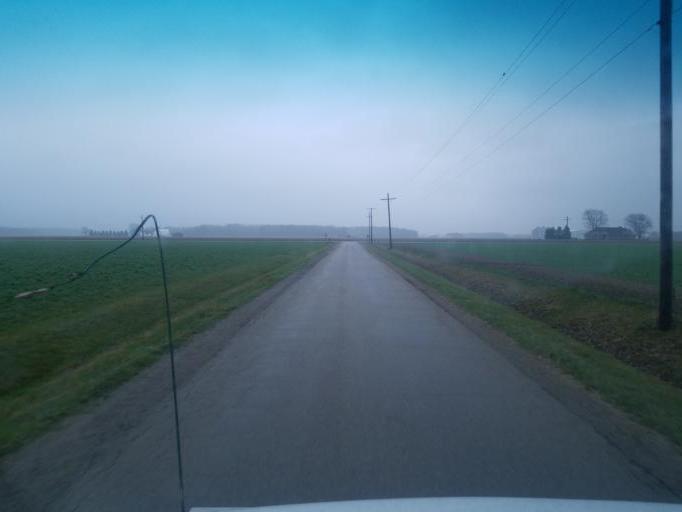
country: US
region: Ohio
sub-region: Fulton County
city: Archbold
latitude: 41.4147
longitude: -84.2476
